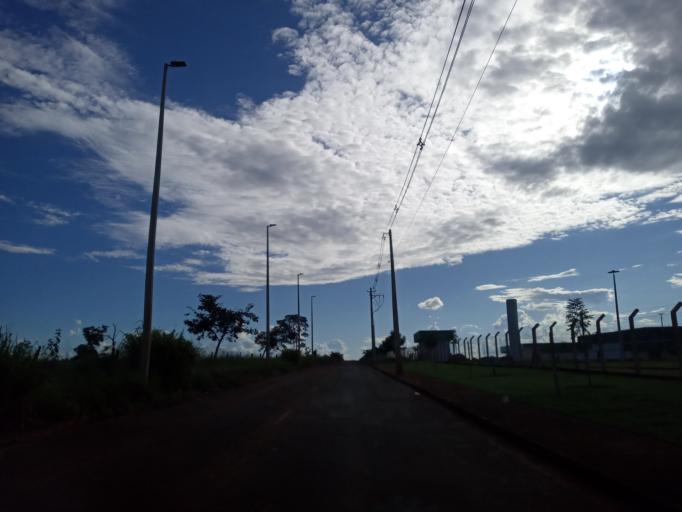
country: BR
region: Minas Gerais
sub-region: Ituiutaba
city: Ituiutaba
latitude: -18.9610
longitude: -49.4958
